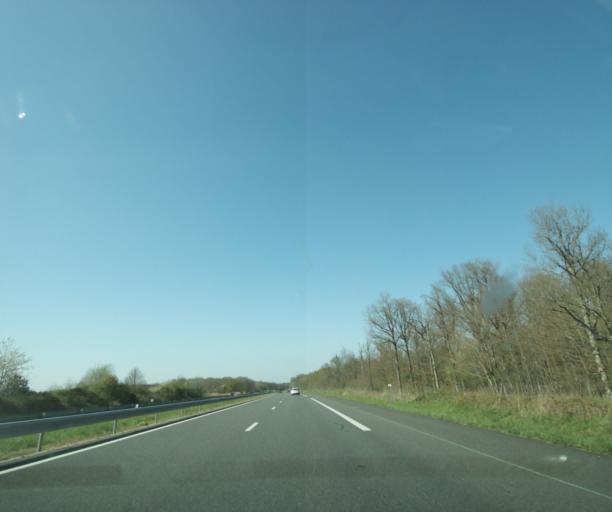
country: FR
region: Centre
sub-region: Departement du Loiret
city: Changy-les-Bois
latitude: 47.8201
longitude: 2.6921
